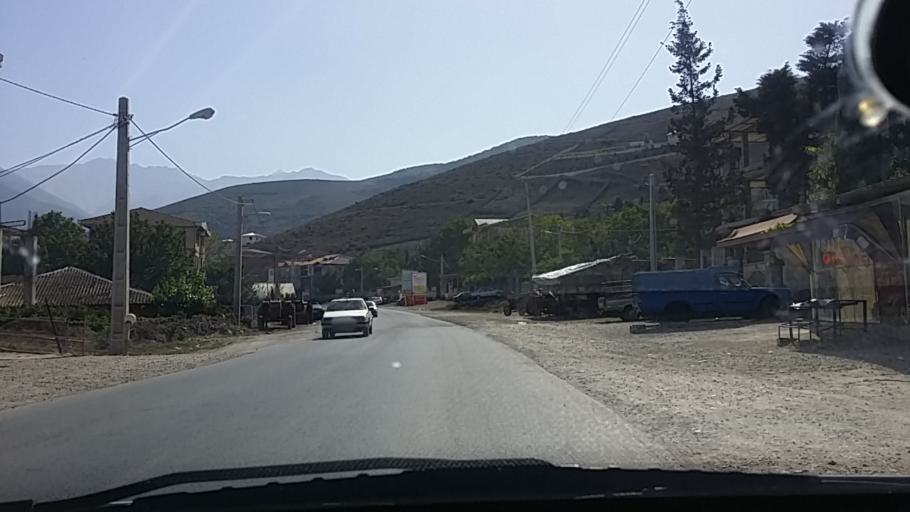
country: IR
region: Mazandaran
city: `Abbasabad
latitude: 36.5292
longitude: 51.1623
